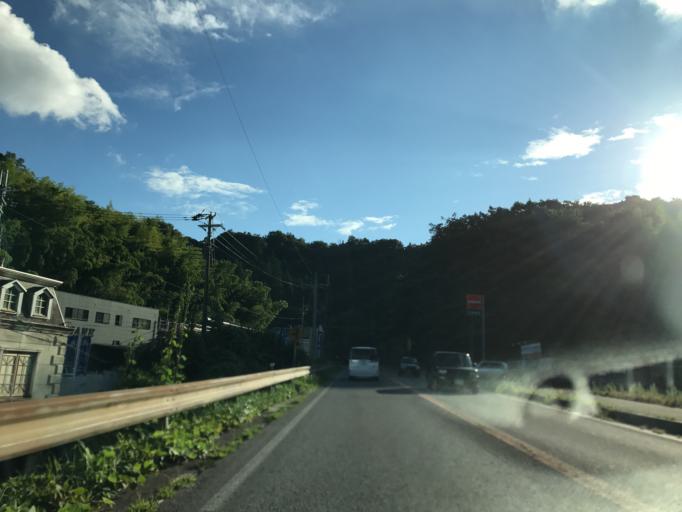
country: JP
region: Shiga Prefecture
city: Hikone
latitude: 35.2777
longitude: 136.2749
